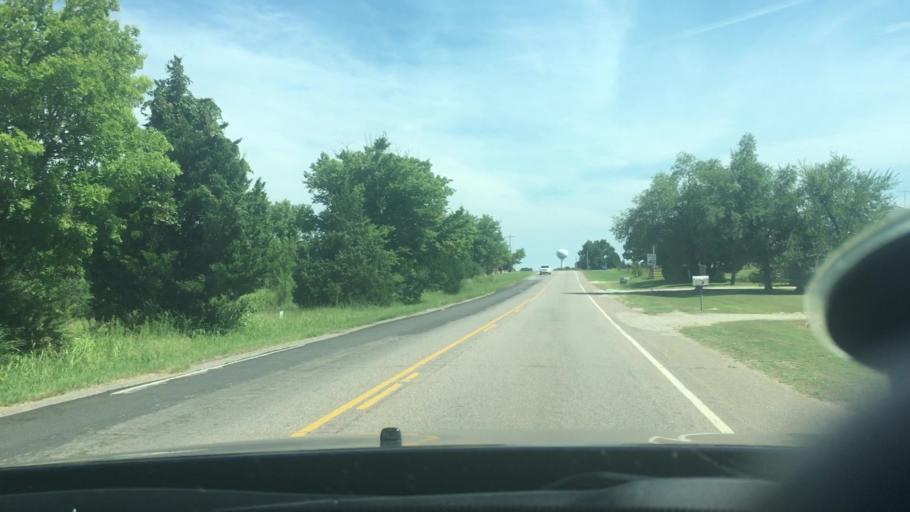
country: US
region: Oklahoma
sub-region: Seminole County
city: Seminole
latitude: 35.2438
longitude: -96.6987
